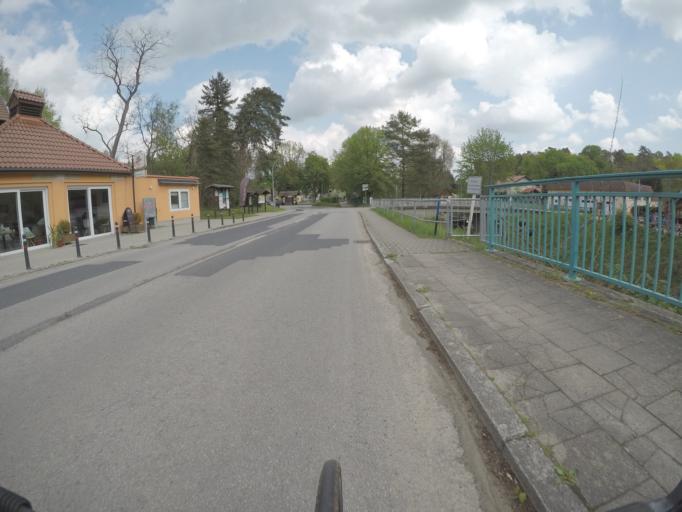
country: DE
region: Brandenburg
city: Marienwerder
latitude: 52.8912
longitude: 13.6385
